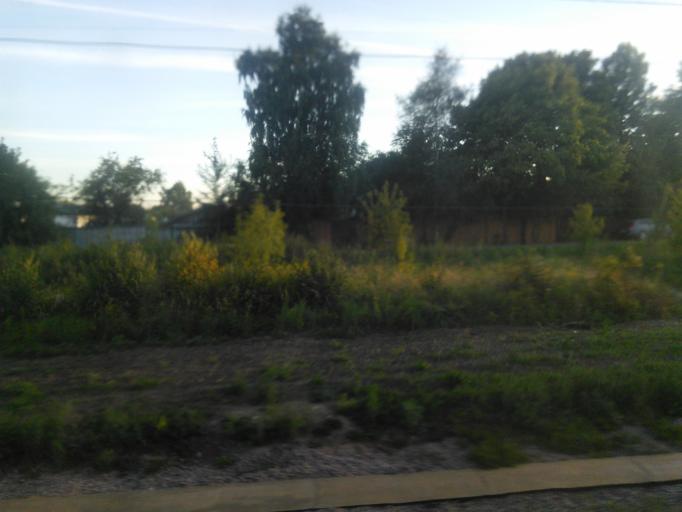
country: RU
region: Moskovskaya
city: Elektrougli
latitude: 55.7327
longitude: 38.1926
